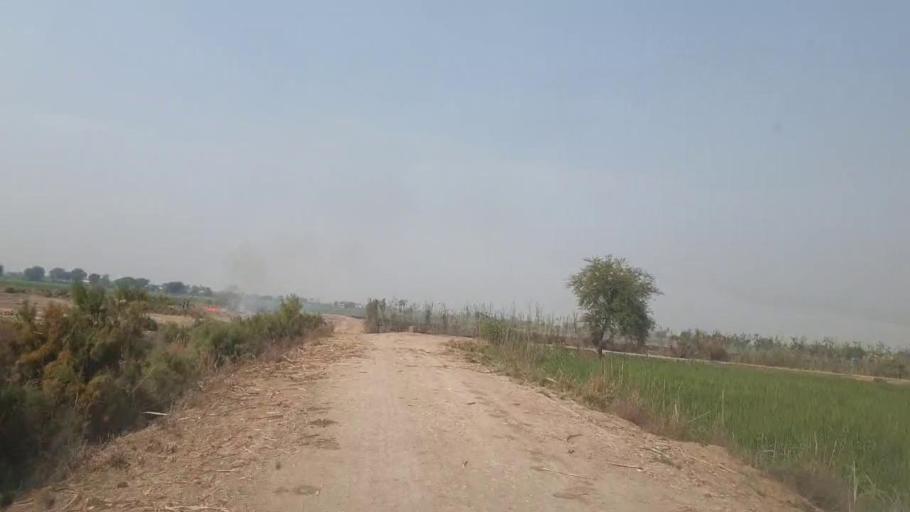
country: PK
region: Sindh
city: Mirpur Khas
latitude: 25.5680
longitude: 69.1330
